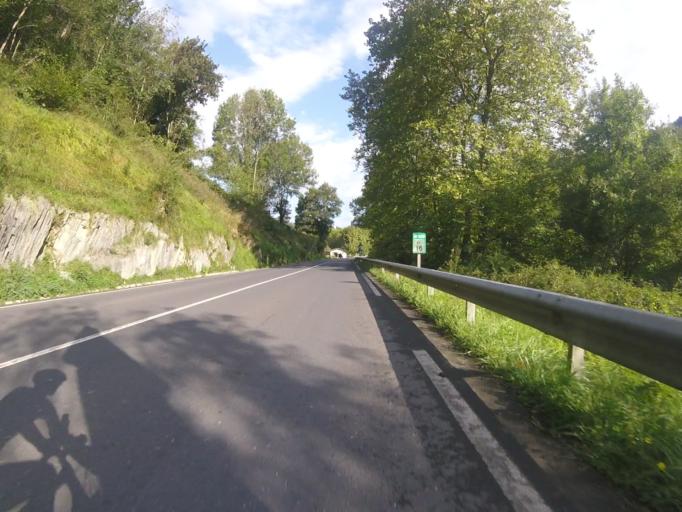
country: ES
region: Basque Country
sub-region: Provincia de Guipuzcoa
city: Orendain
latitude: 43.0740
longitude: -2.0869
